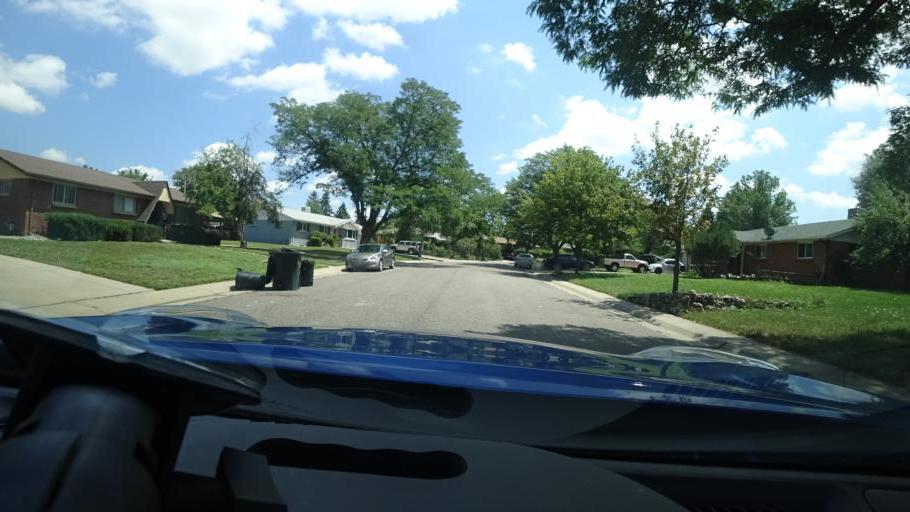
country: US
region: Colorado
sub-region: Adams County
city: Aurora
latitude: 39.7061
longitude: -104.8464
